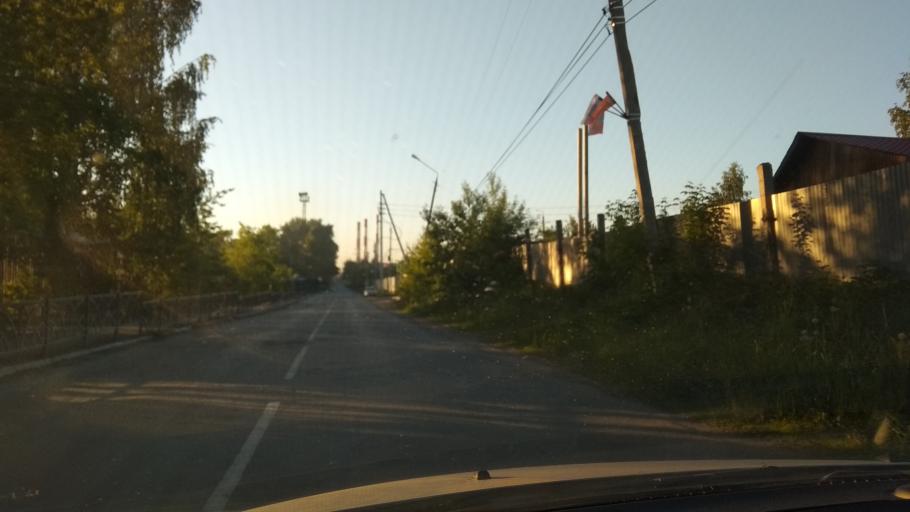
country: RU
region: Sverdlovsk
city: Sredneuralsk
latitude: 56.9836
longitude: 60.4598
